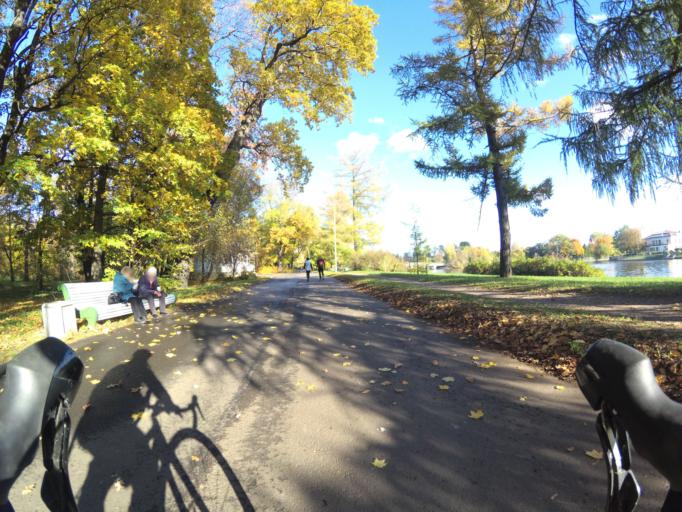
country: RU
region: Leningrad
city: Krestovskiy ostrov
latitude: 59.9761
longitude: 30.2683
